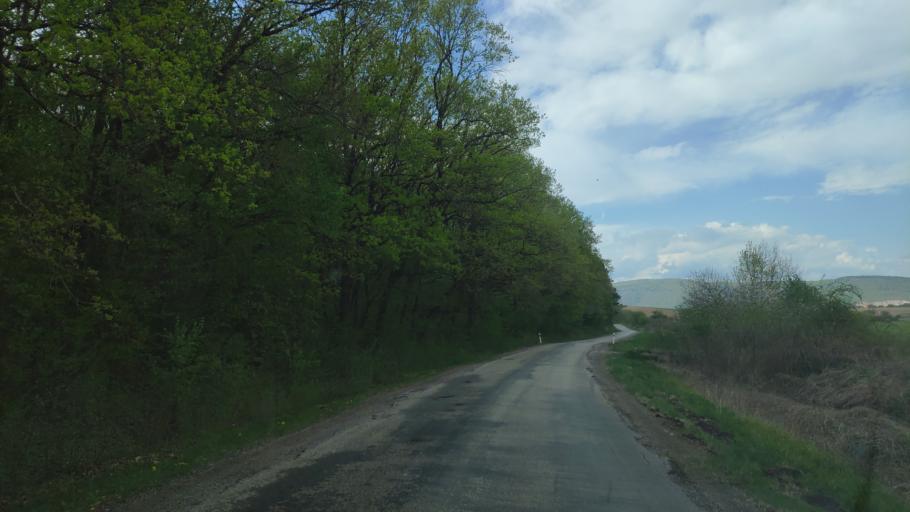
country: SK
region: Kosicky
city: Moldava nad Bodvou
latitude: 48.5704
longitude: 20.9338
